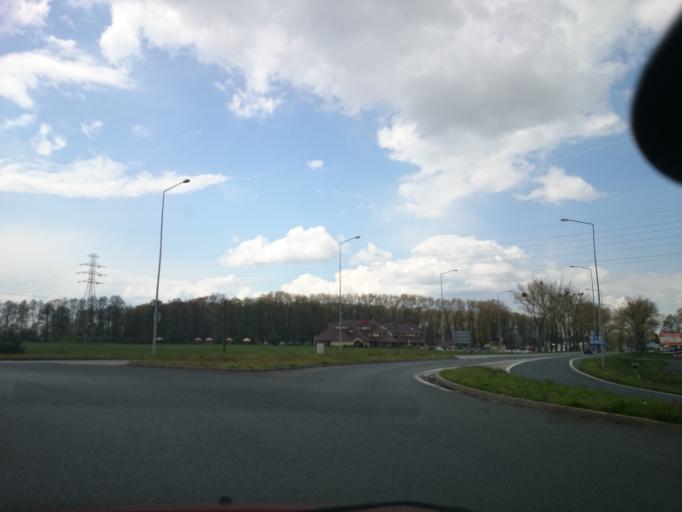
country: PL
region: Opole Voivodeship
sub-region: Powiat opolski
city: Opole
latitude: 50.6414
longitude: 17.9952
